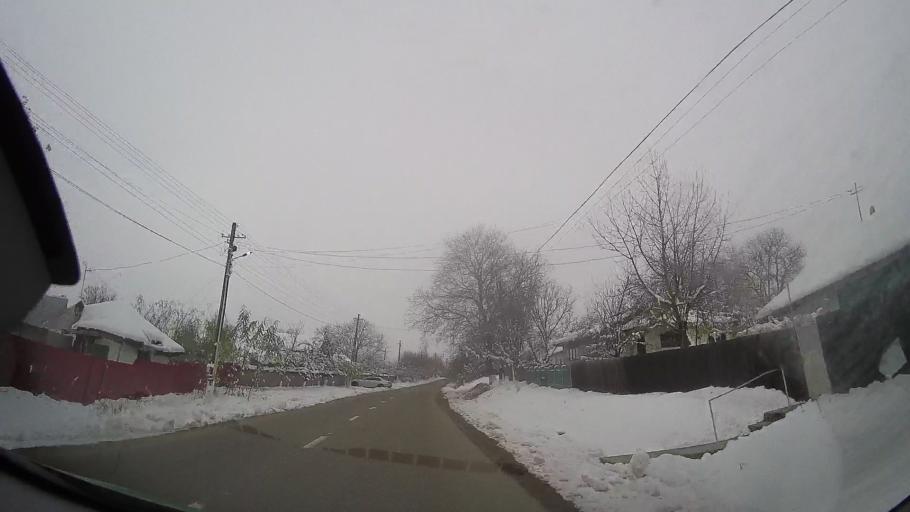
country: RO
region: Neamt
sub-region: Comuna Oniceni
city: Oniceni
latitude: 46.8074
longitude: 27.1827
